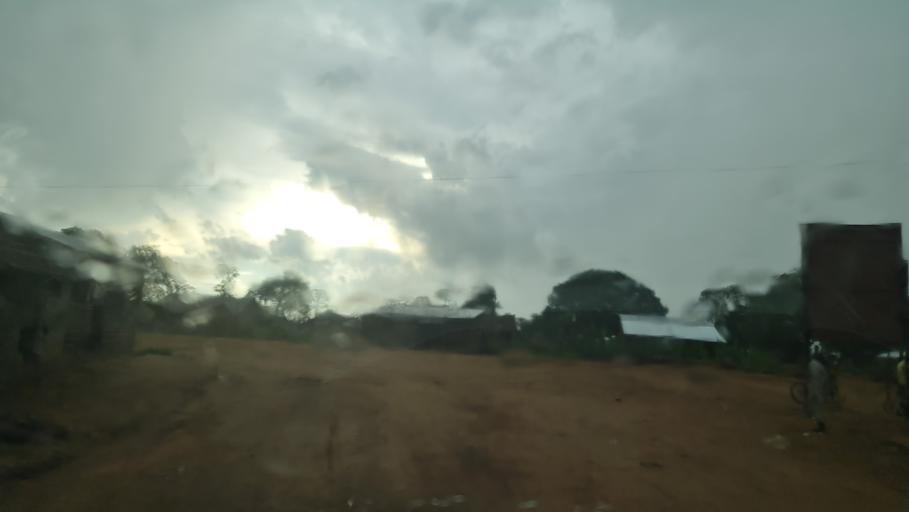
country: MZ
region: Nampula
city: Nacala
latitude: -14.0042
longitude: 40.3492
